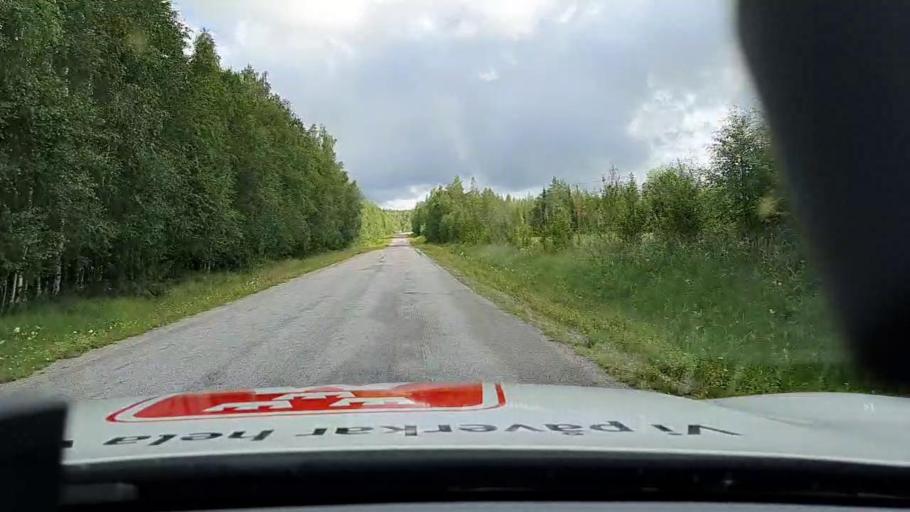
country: SE
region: Norrbotten
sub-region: Overkalix Kommun
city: OEverkalix
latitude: 66.2550
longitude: 23.0185
